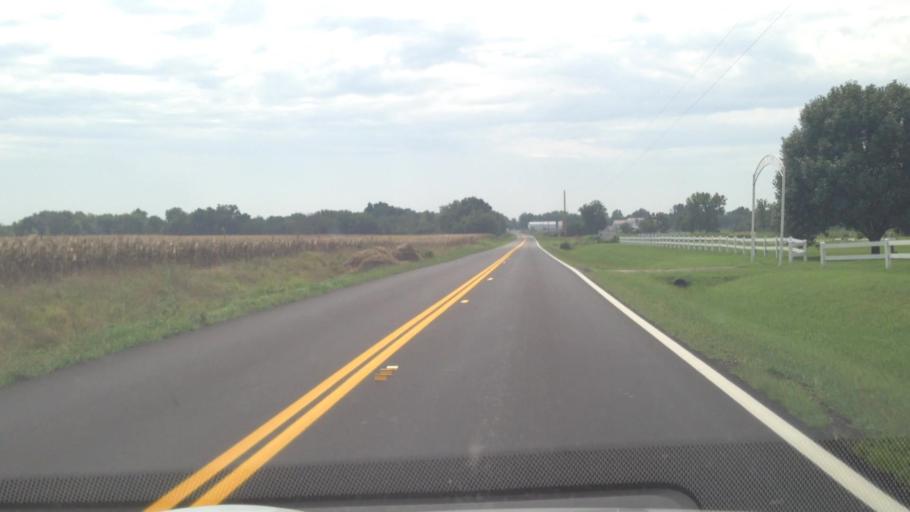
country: US
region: Kansas
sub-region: Crawford County
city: Girard
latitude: 37.6704
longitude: -94.9697
